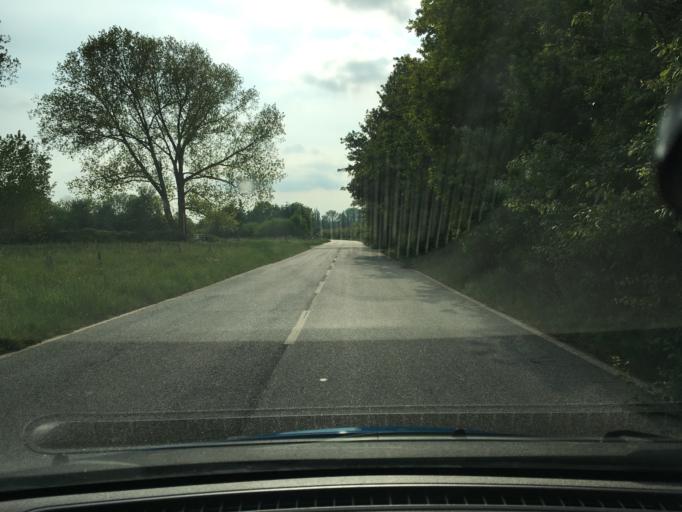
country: DE
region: Hamburg
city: Rothenburgsort
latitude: 53.4809
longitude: 10.0508
